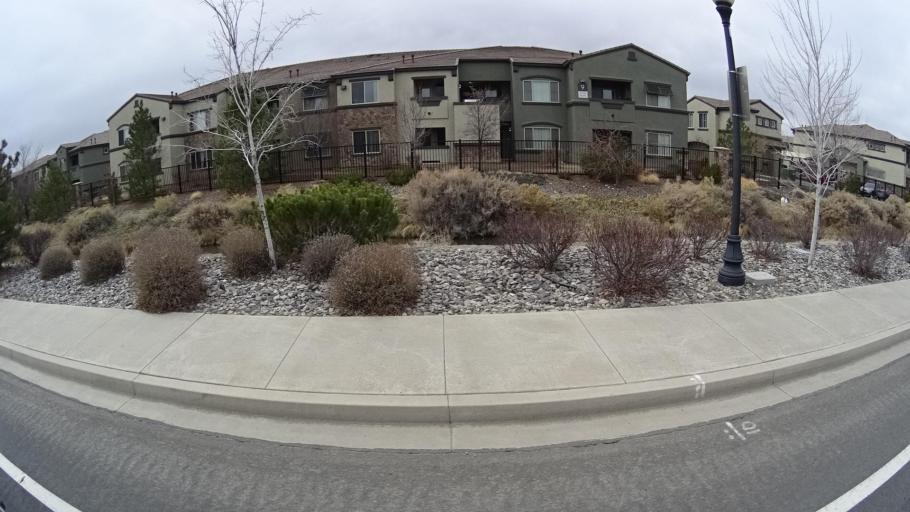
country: US
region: Nevada
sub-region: Washoe County
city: Spanish Springs
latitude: 39.6126
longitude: -119.7014
